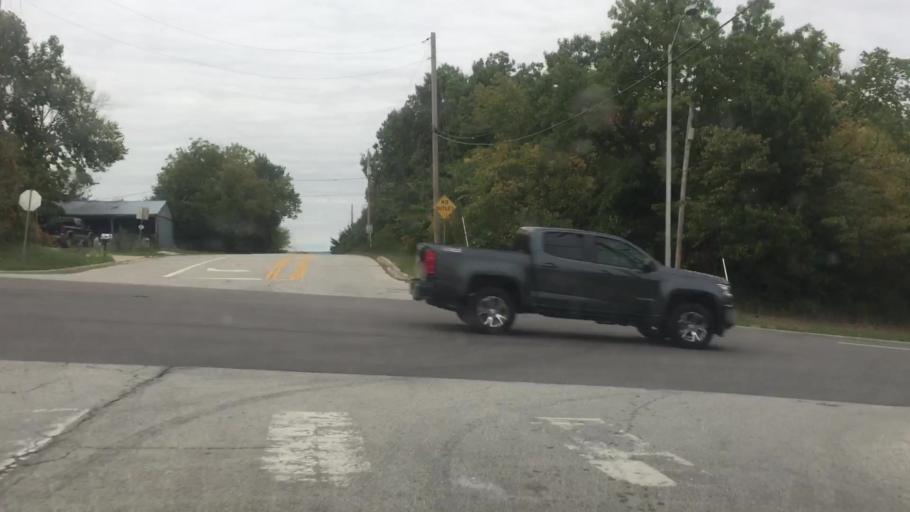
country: US
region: Kansas
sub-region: Johnson County
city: Shawnee
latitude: 39.0219
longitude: -94.7705
